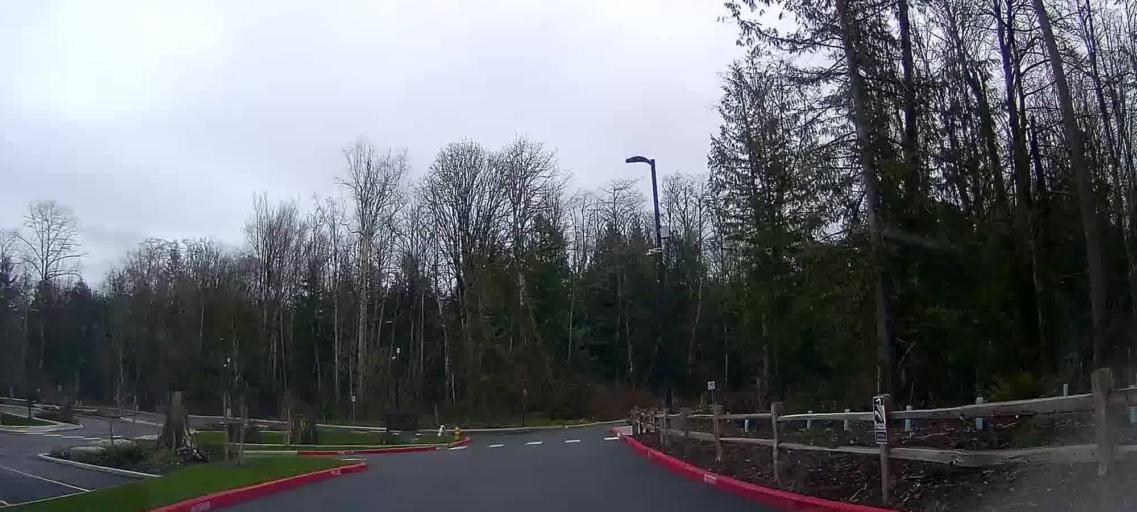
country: US
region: Washington
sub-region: Skagit County
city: Big Lake
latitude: 48.4230
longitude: -122.2732
